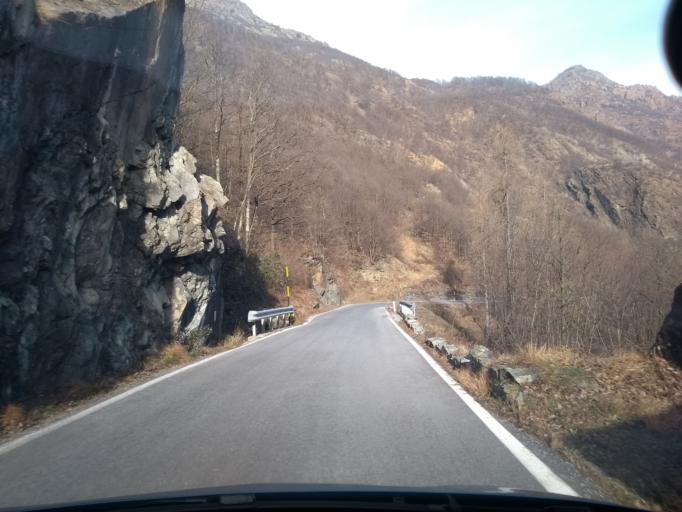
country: IT
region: Piedmont
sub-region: Provincia di Torino
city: Ala di Stura
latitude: 45.3164
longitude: 7.3316
